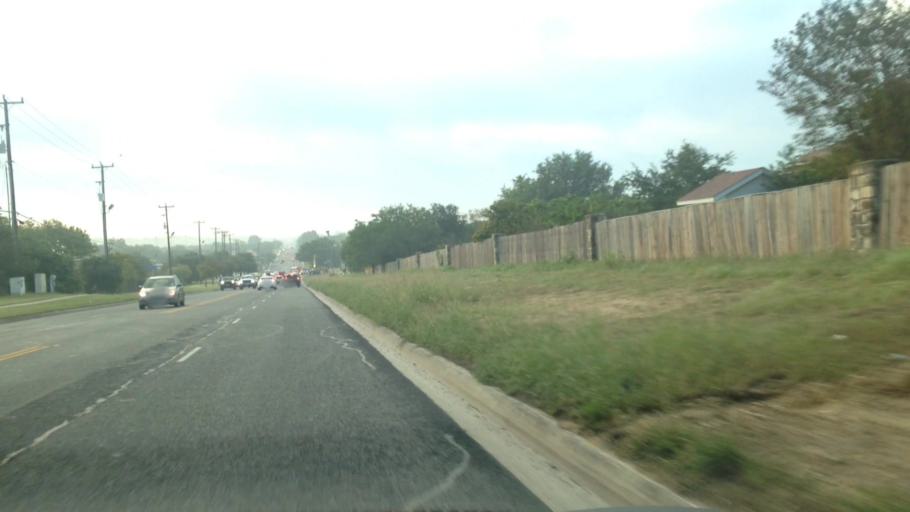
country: US
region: Texas
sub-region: Bexar County
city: Live Oak
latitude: 29.5813
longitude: -98.3748
